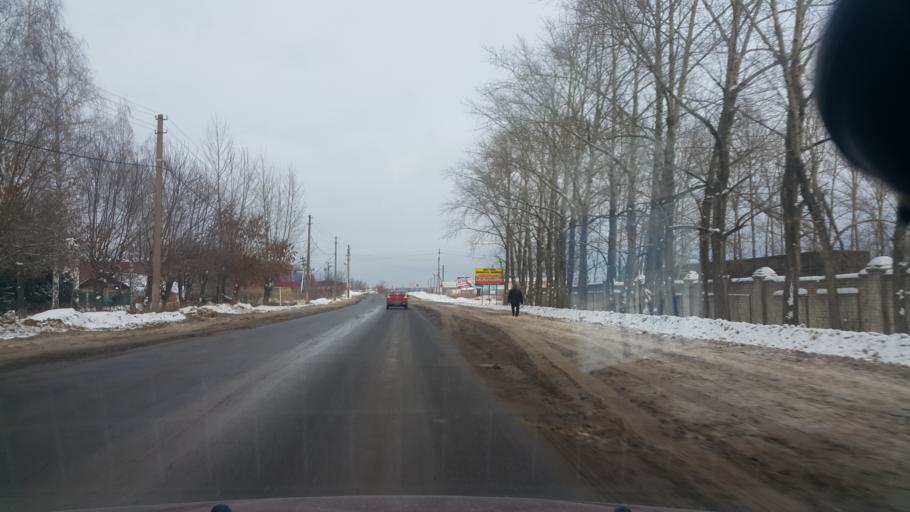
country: RU
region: Tambov
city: Pokrovo-Prigorodnoye
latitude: 52.6578
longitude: 41.4297
